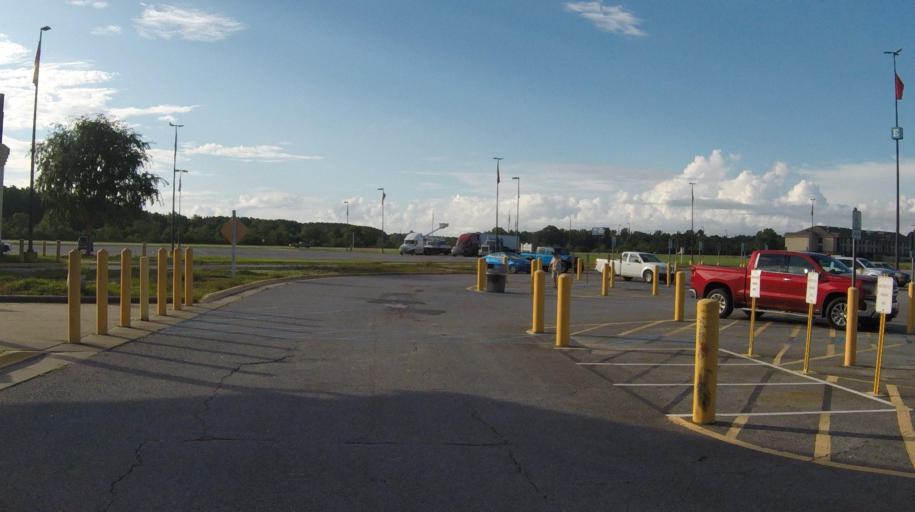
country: US
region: Louisiana
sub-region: Allen Parish
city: Kinder
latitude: 30.5442
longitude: -92.8147
